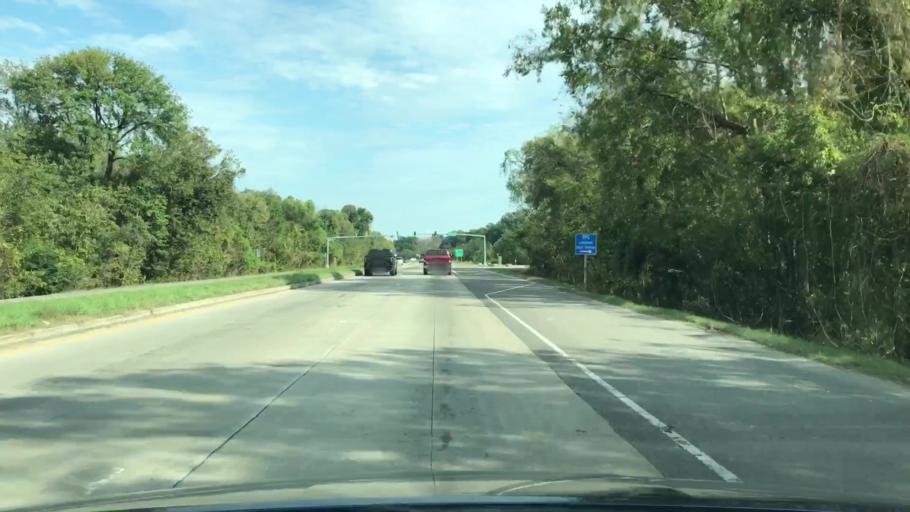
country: US
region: Louisiana
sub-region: Jefferson Parish
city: Avondale
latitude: 29.9093
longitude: -90.1933
